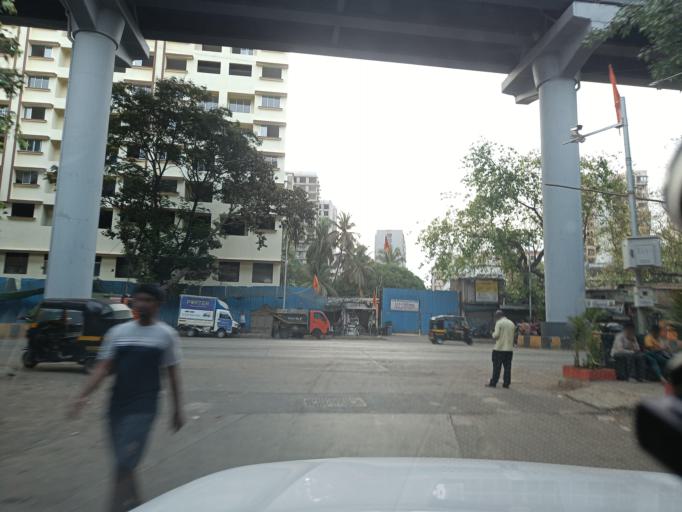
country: IN
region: Maharashtra
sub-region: Mumbai Suburban
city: Powai
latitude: 19.1266
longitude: 72.8307
